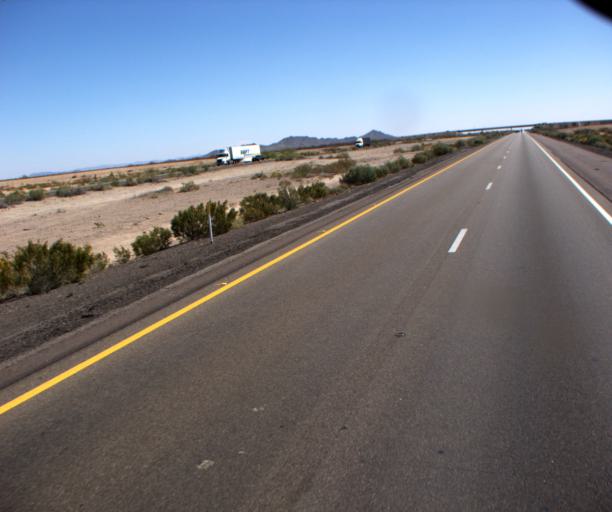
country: US
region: Arizona
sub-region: La Paz County
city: Salome
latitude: 33.5962
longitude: -113.5355
